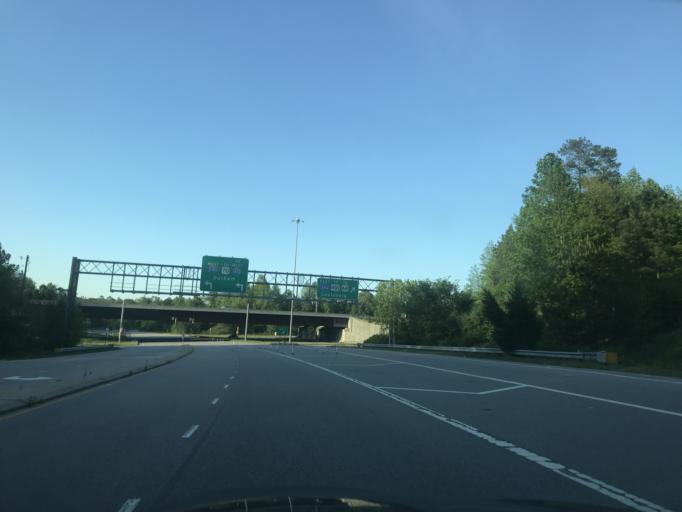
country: US
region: North Carolina
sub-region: Wake County
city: Raleigh
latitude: 35.8720
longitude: -78.5690
